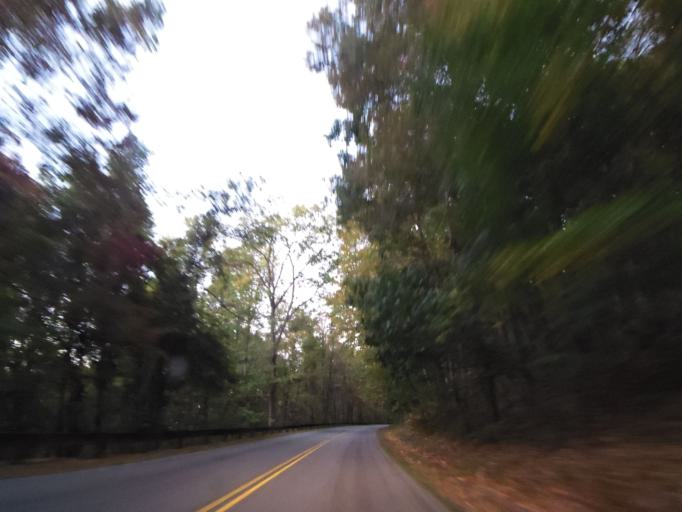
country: US
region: Tennessee
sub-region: Blount County
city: Wildwood
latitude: 35.6938
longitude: -83.8792
